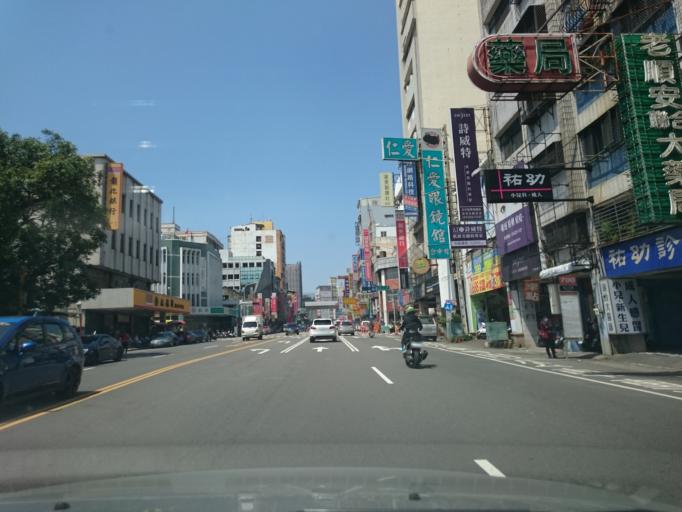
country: TW
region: Taiwan
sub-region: Taichung City
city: Taichung
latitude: 24.1327
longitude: 120.6839
